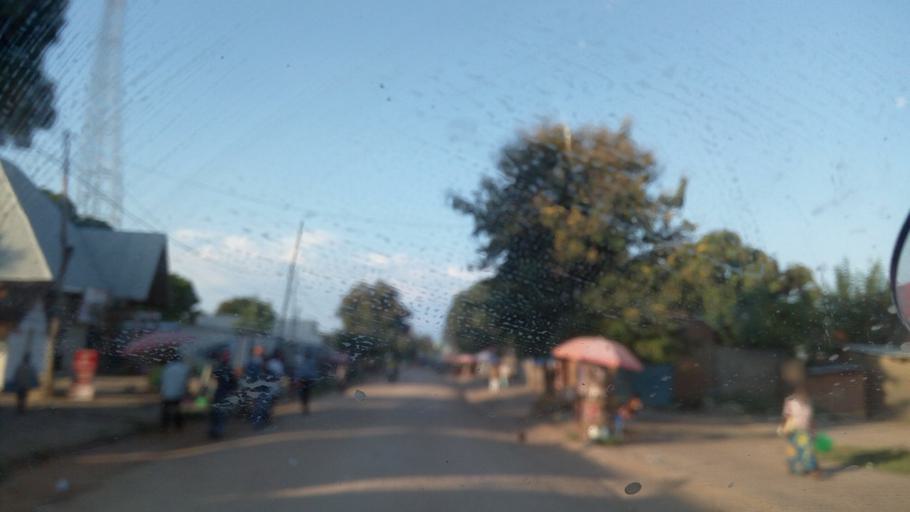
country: BI
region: Bururi
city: Rumonge
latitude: -4.1103
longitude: 29.0898
